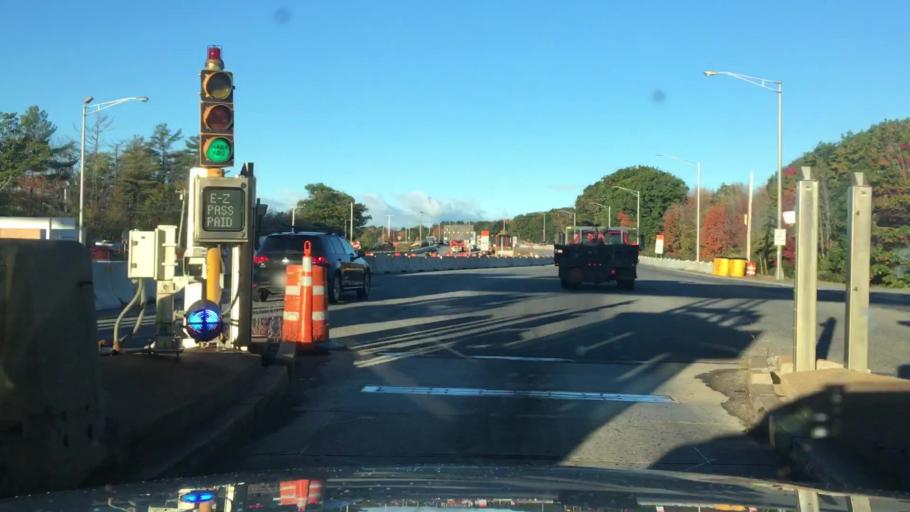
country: US
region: Maine
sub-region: Cumberland County
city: South Portland Gardens
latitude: 43.6258
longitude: -70.3427
